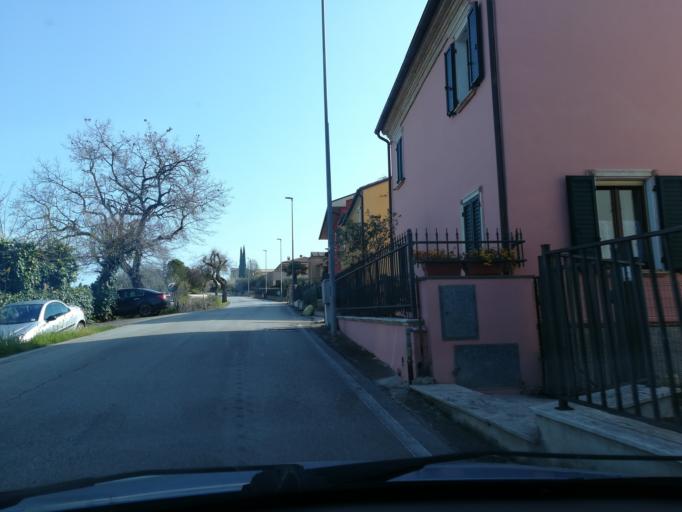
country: IT
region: The Marches
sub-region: Provincia di Macerata
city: Villa Potenza
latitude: 43.3242
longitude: 13.4437
